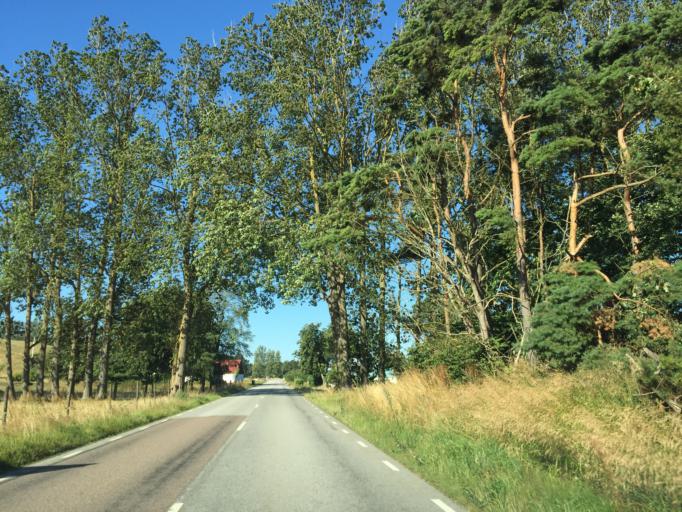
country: SE
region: Skane
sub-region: Ystads Kommun
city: Kopingebro
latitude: 55.3914
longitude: 14.1071
